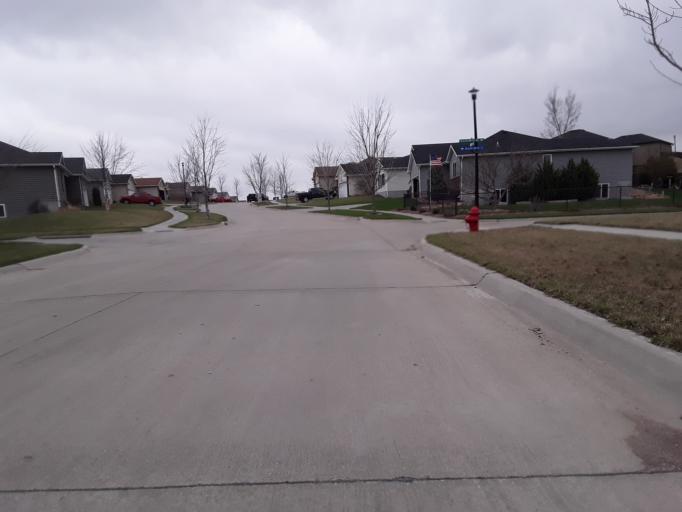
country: US
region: Nebraska
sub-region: Lancaster County
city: Lincoln
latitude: 40.8429
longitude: -96.5983
